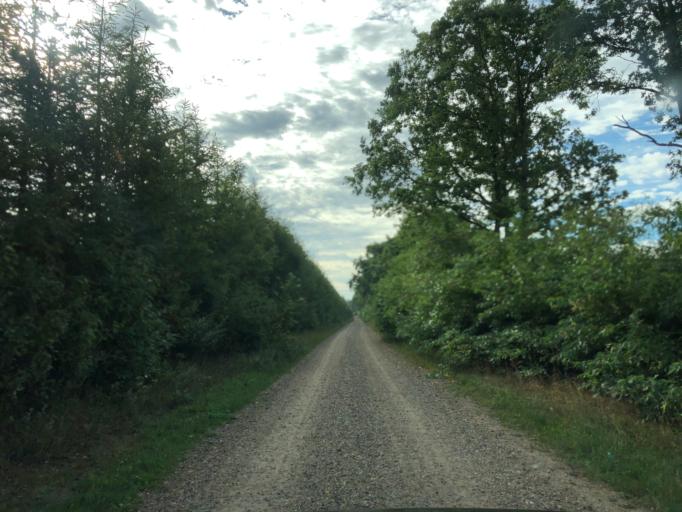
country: DK
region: Central Jutland
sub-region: Holstebro Kommune
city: Ulfborg
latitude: 56.1871
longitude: 8.3410
